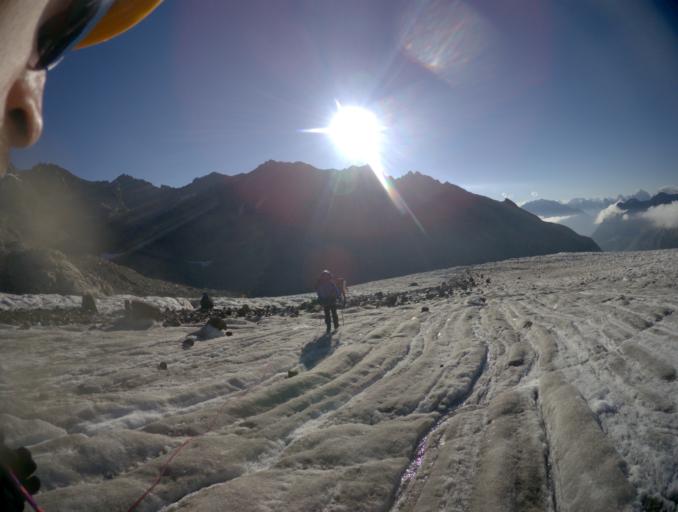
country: RU
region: Kabardino-Balkariya
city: Terskol
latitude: 43.3207
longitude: 42.5229
